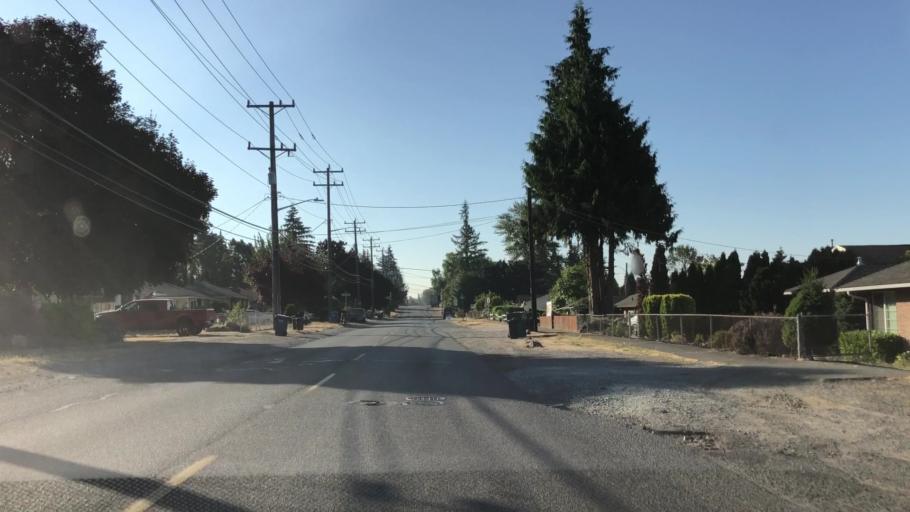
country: US
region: Washington
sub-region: King County
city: Tukwila
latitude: 47.5011
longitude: -122.2688
